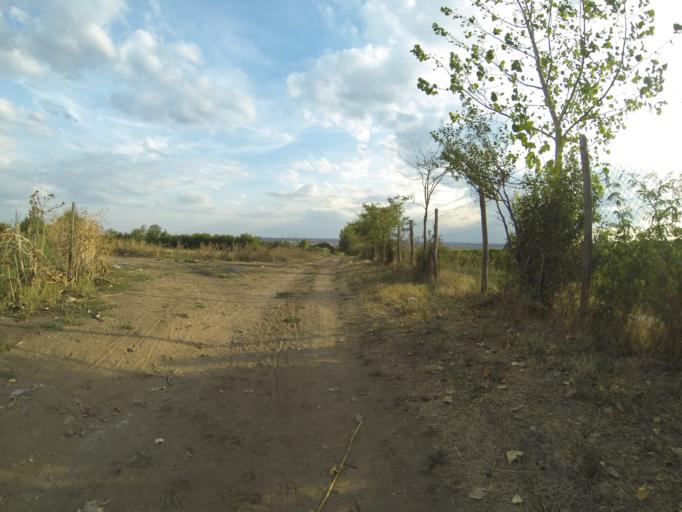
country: RO
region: Dolj
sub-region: Comuna Segarcea
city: Segarcea
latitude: 44.1044
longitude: 23.7265
